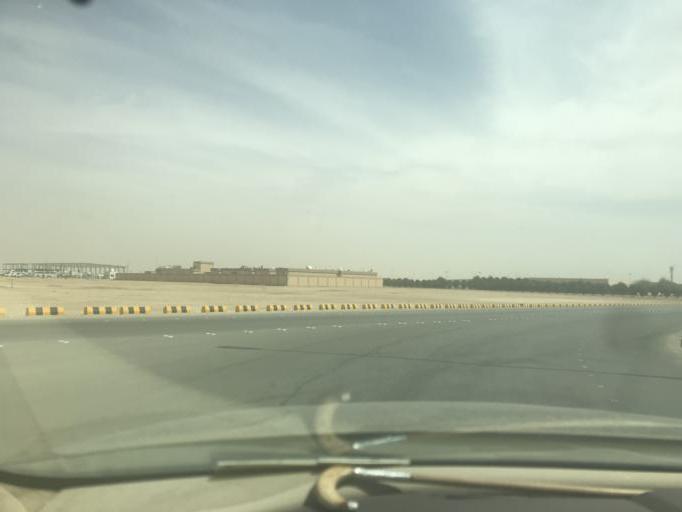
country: SA
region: Ar Riyad
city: Riyadh
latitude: 24.9842
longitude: 46.6830
